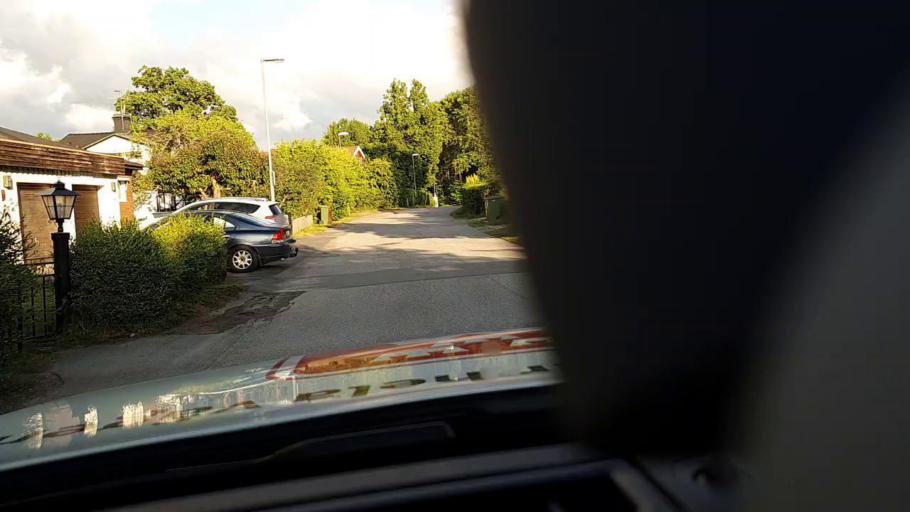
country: SE
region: Stockholm
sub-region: Huddinge Kommun
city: Huddinge
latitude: 59.2455
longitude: 17.9727
